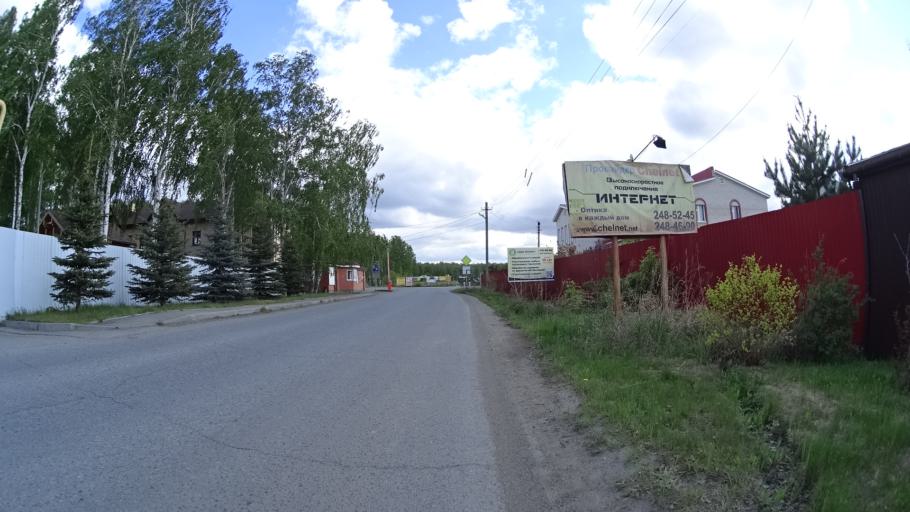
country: RU
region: Chelyabinsk
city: Sargazy
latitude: 55.1430
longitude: 61.2301
